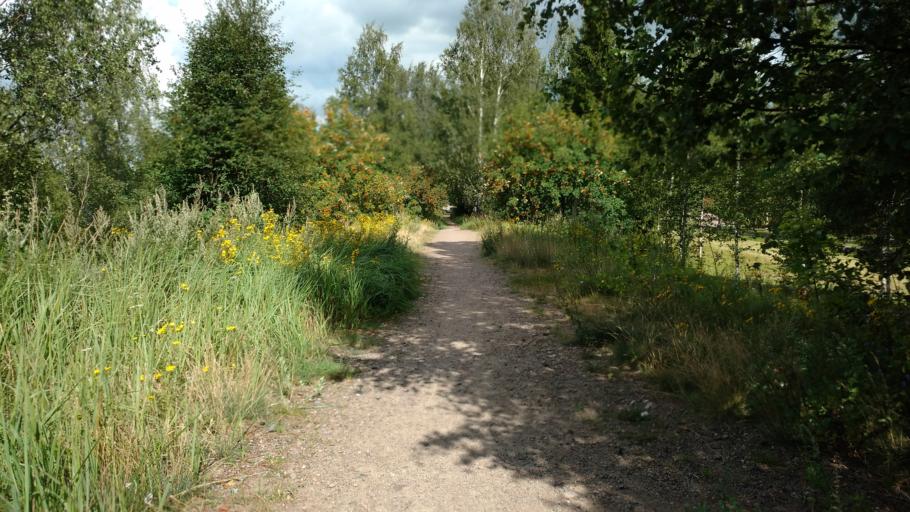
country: FI
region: Varsinais-Suomi
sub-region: Salo
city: Salo
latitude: 60.3665
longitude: 23.1248
